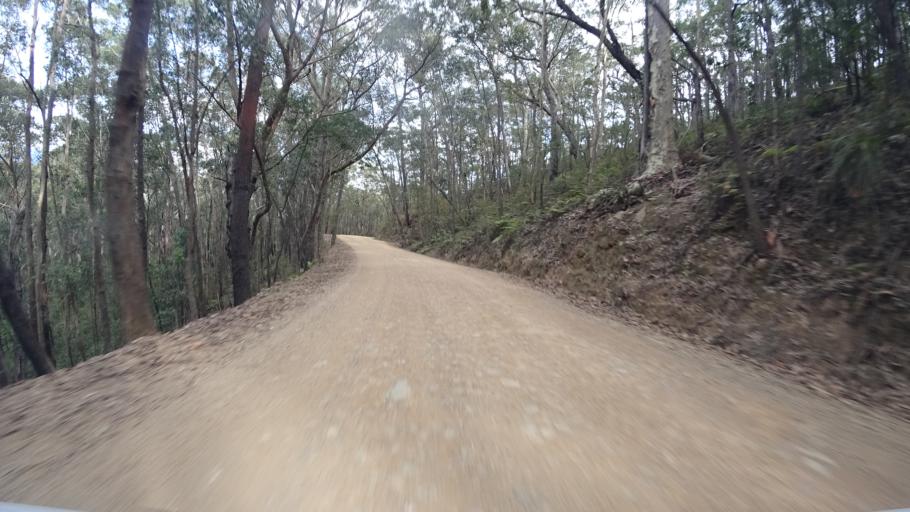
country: AU
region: New South Wales
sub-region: Shoalhaven Shire
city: Milton
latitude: -35.3566
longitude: 150.2193
